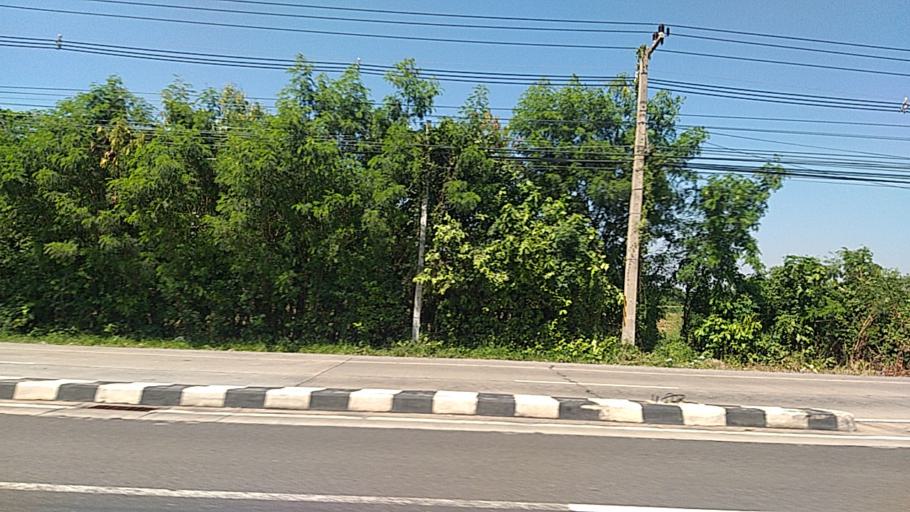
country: TH
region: Nakhon Ratchasima
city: Kham Thale So
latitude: 14.9364
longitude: 101.9883
